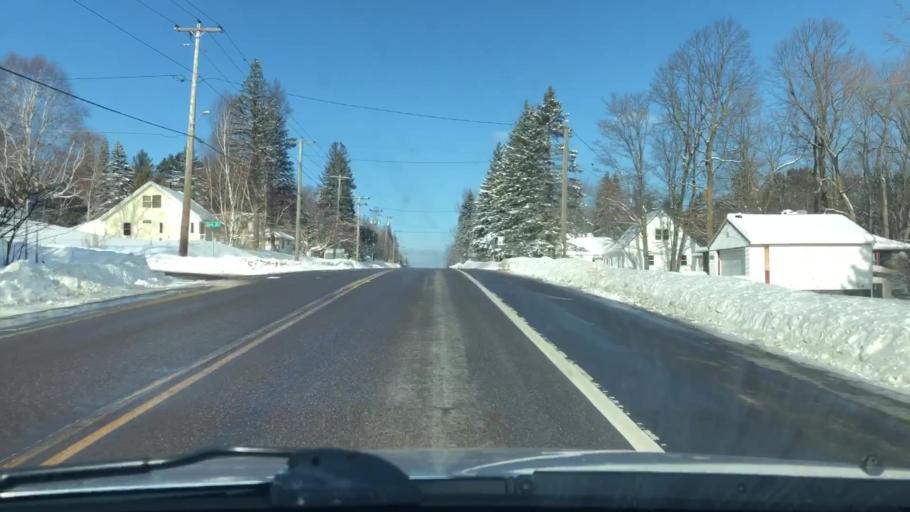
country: US
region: Minnesota
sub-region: Saint Louis County
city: Duluth
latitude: 46.8127
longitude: -92.1322
